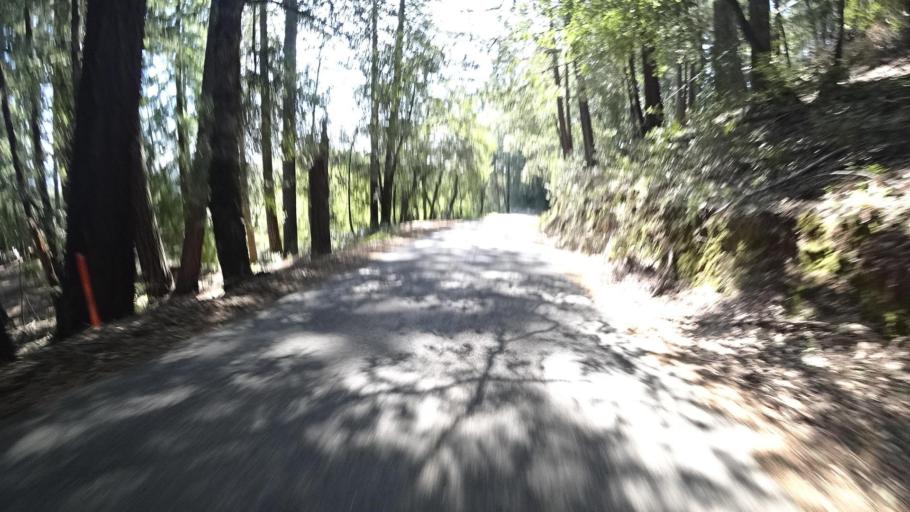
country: US
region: California
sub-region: Humboldt County
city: Redway
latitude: 40.0853
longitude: -123.6617
